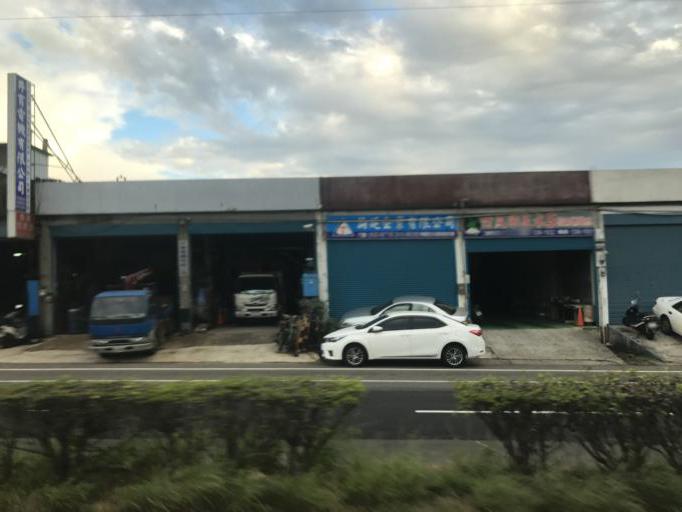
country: TW
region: Taiwan
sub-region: Hsinchu
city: Hsinchu
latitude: 24.7908
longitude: 120.9361
